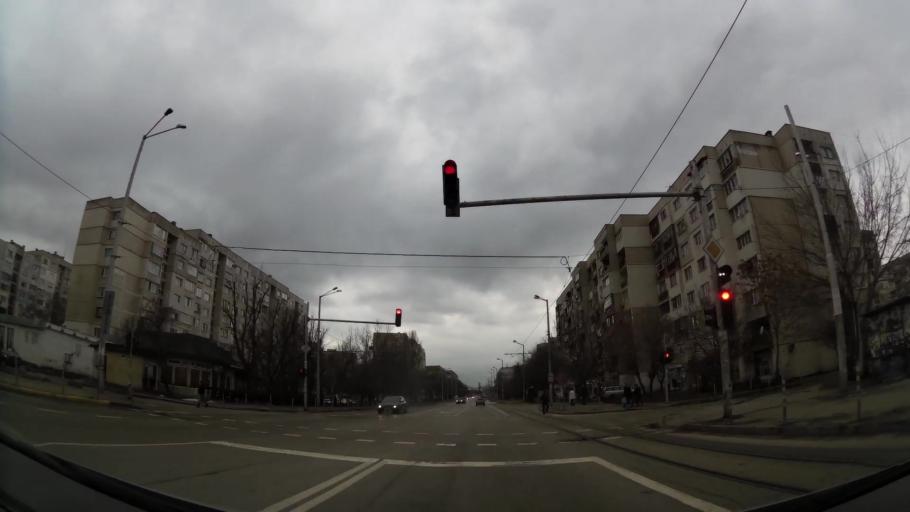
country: BG
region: Sofia-Capital
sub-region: Stolichna Obshtina
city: Sofia
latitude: 42.7347
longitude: 23.2916
